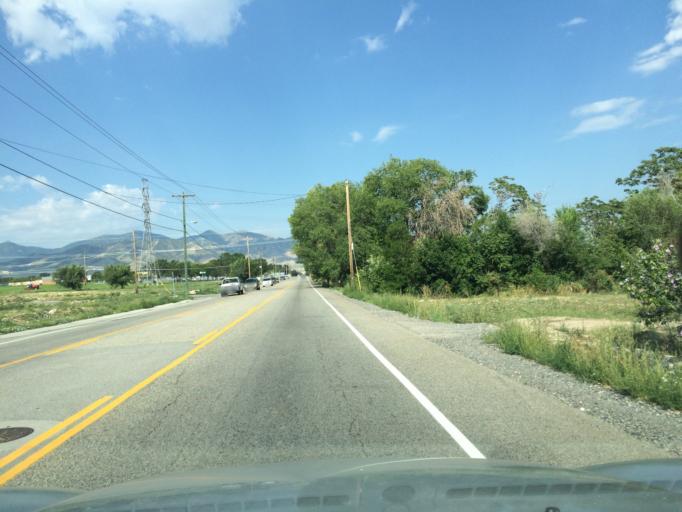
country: US
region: Utah
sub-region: Salt Lake County
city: West Valley City
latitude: 40.6966
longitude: -112.0274
